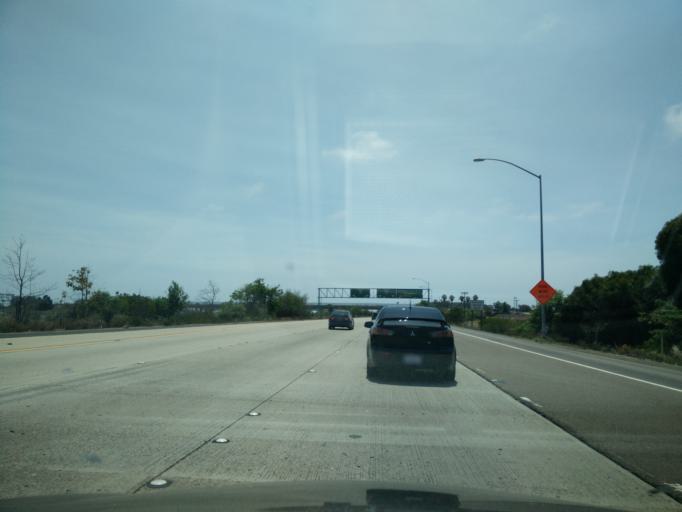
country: US
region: California
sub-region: San Diego County
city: Chula Vista
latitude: 32.6547
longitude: -117.0936
